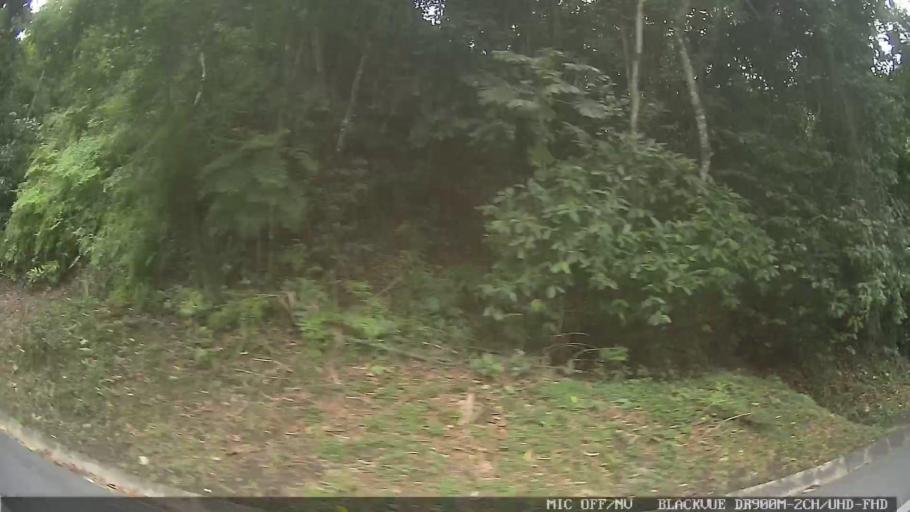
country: BR
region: Sao Paulo
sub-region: Caraguatatuba
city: Caraguatatuba
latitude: -23.6045
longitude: -45.4478
